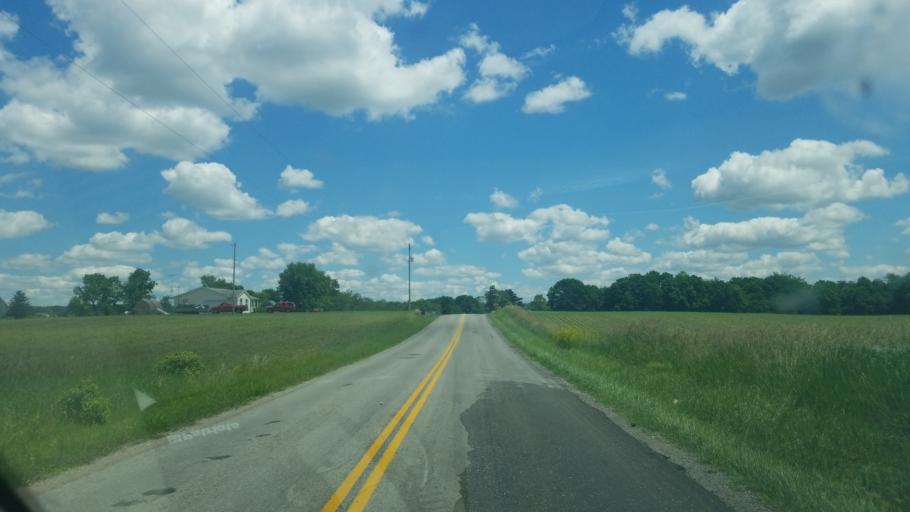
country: US
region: Ohio
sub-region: Ashland County
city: Ashland
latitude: 40.9533
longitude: -82.3681
